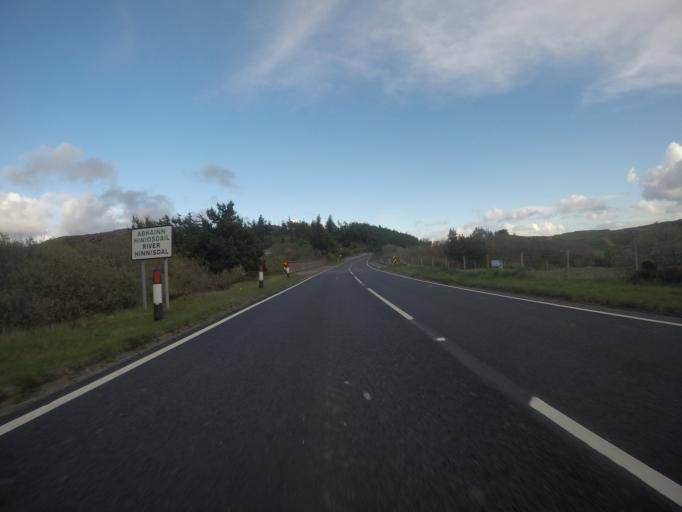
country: GB
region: Scotland
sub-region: Highland
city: Portree
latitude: 57.5311
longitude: -6.3507
